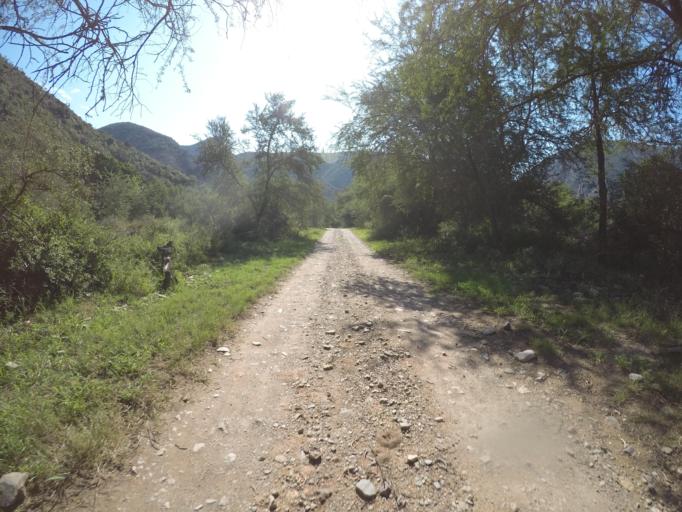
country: ZA
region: Eastern Cape
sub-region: Cacadu District Municipality
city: Kareedouw
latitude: -33.6566
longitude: 24.3658
